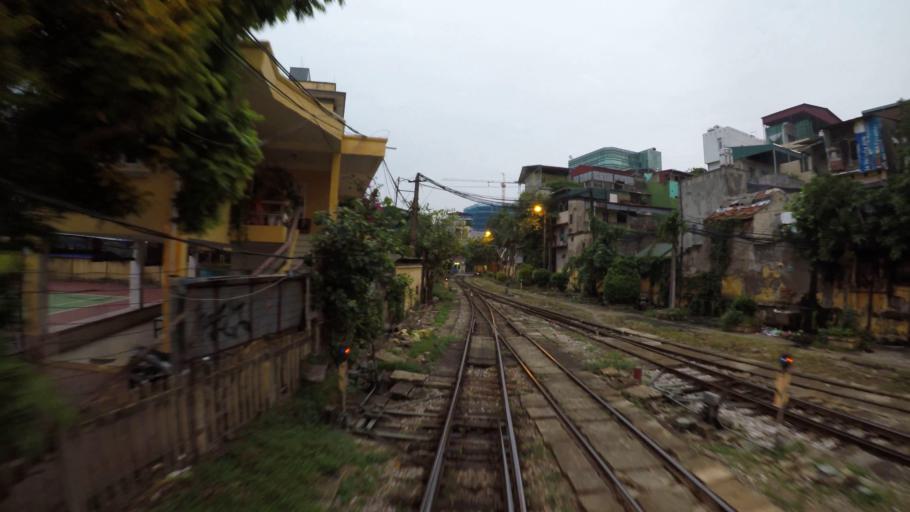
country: VN
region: Ha Noi
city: Hoan Kiem
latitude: 21.0312
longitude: 105.8456
